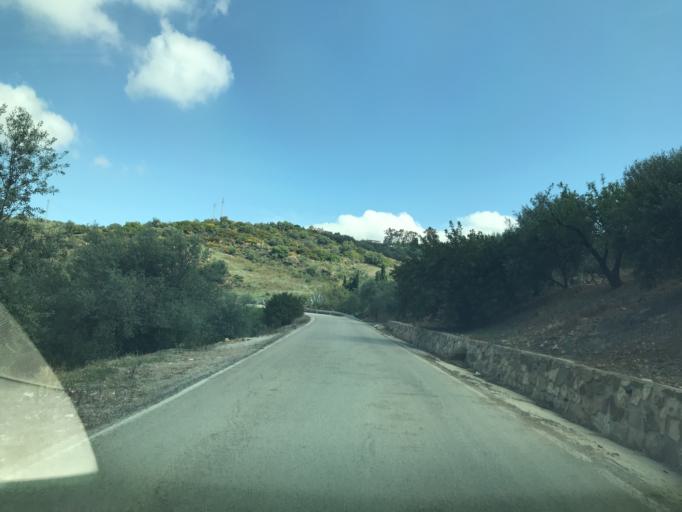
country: ES
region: Andalusia
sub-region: Provincia de Malaga
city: Periana
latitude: 36.9232
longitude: -4.1772
